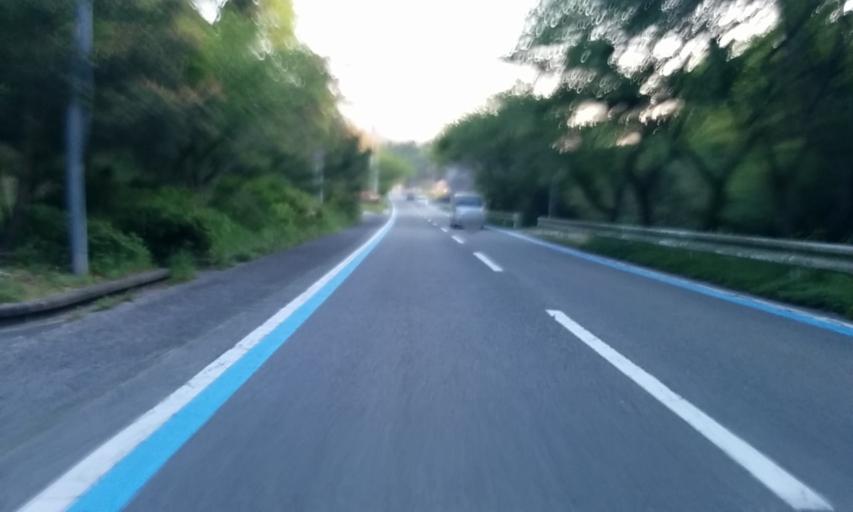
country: JP
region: Ehime
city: Iyo
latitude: 33.7098
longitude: 132.6659
